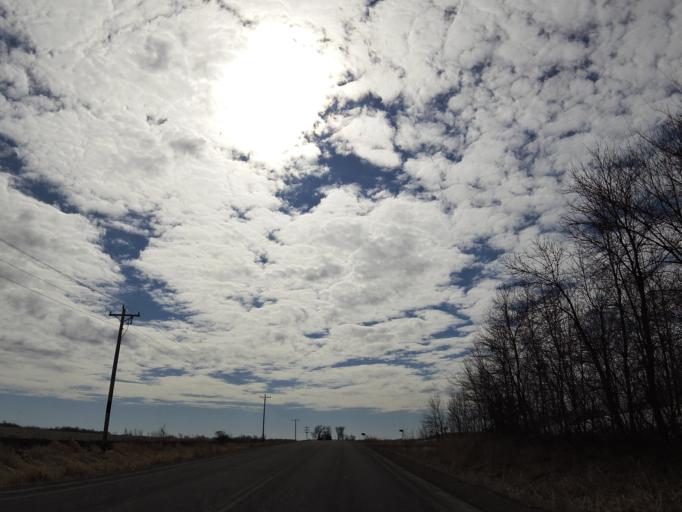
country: US
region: Minnesota
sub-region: Le Sueur County
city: New Prague
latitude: 44.5649
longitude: -93.5570
